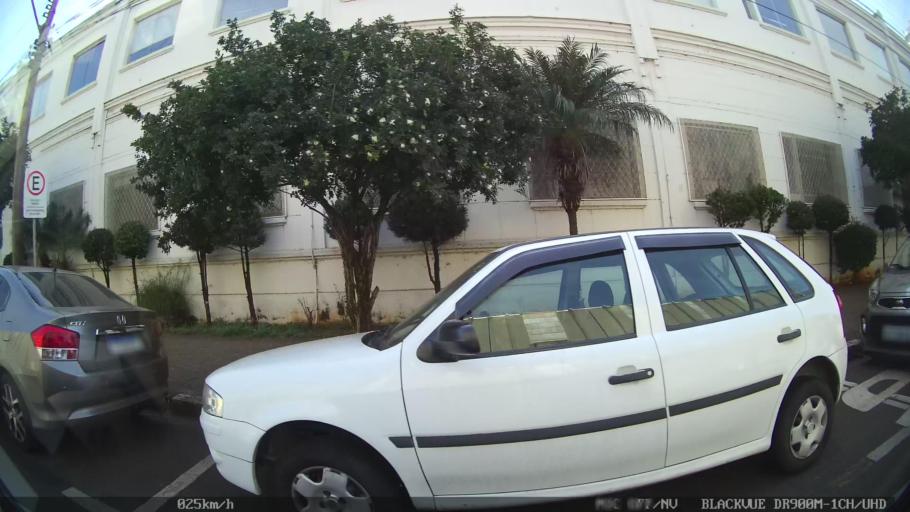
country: BR
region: Sao Paulo
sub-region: Piracicaba
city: Piracicaba
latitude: -22.7066
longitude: -47.6559
